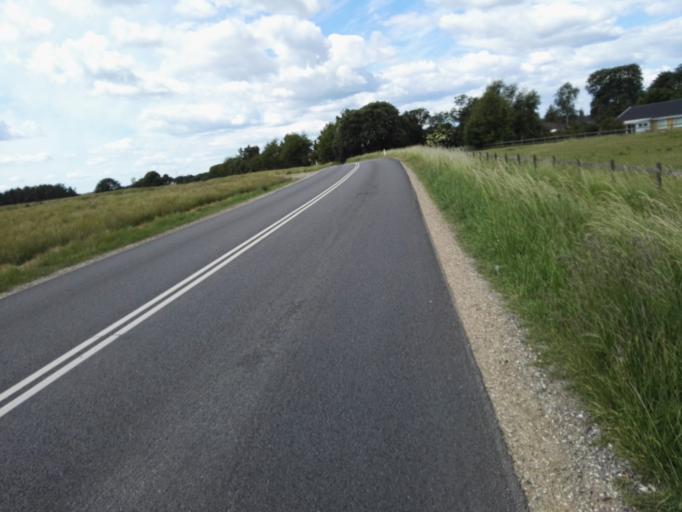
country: DK
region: Capital Region
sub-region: Egedal Kommune
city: Stenlose
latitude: 55.7665
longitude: 12.1721
